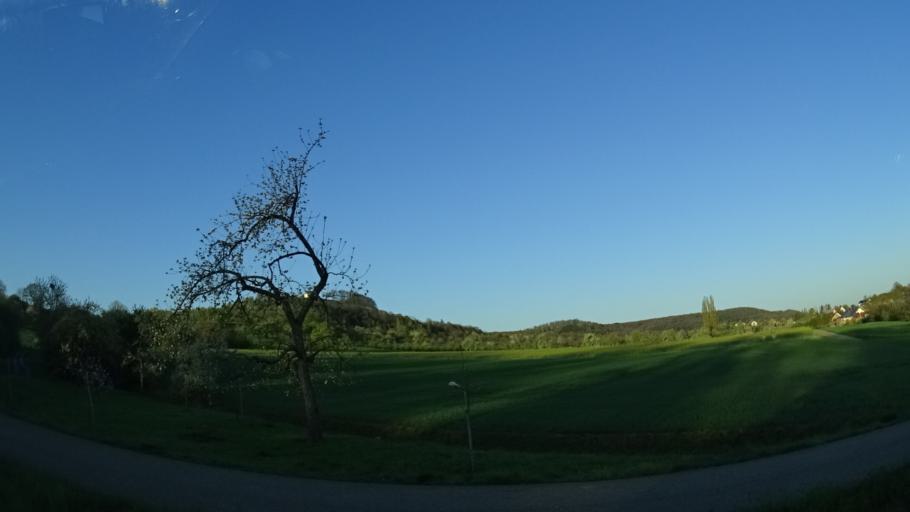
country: DE
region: Baden-Wuerttemberg
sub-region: Regierungsbezirk Stuttgart
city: Pfedelbach
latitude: 49.1718
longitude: 9.5110
